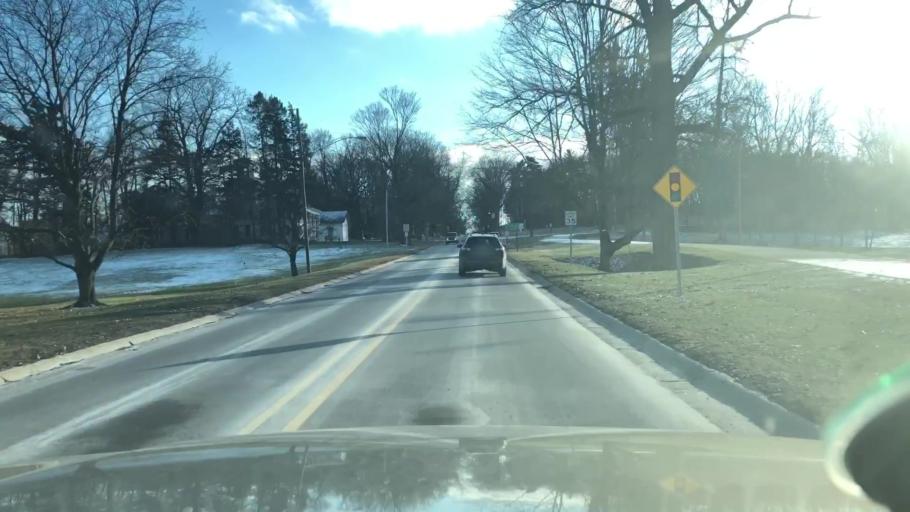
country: US
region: Michigan
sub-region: Jackson County
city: Jackson
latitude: 42.2164
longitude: -84.4182
